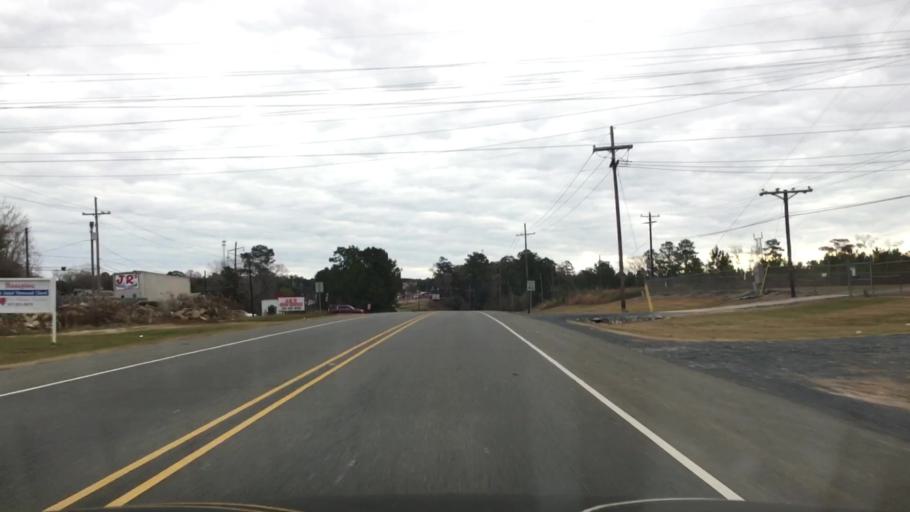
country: US
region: Louisiana
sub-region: Vernon Parish
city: Fort Polk South
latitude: 31.0565
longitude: -93.2525
